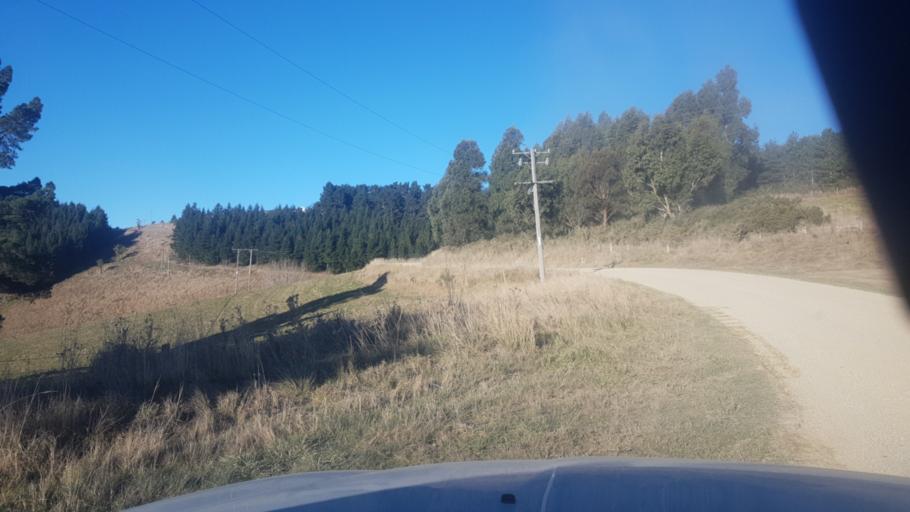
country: NZ
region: Canterbury
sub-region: Timaru District
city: Pleasant Point
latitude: -44.3428
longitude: 171.0718
